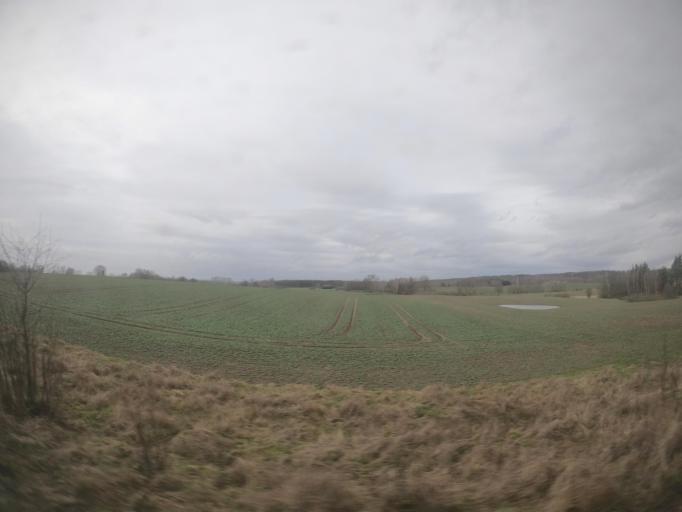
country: PL
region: West Pomeranian Voivodeship
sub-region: Powiat szczecinecki
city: Szczecinek
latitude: 53.7169
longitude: 16.7701
